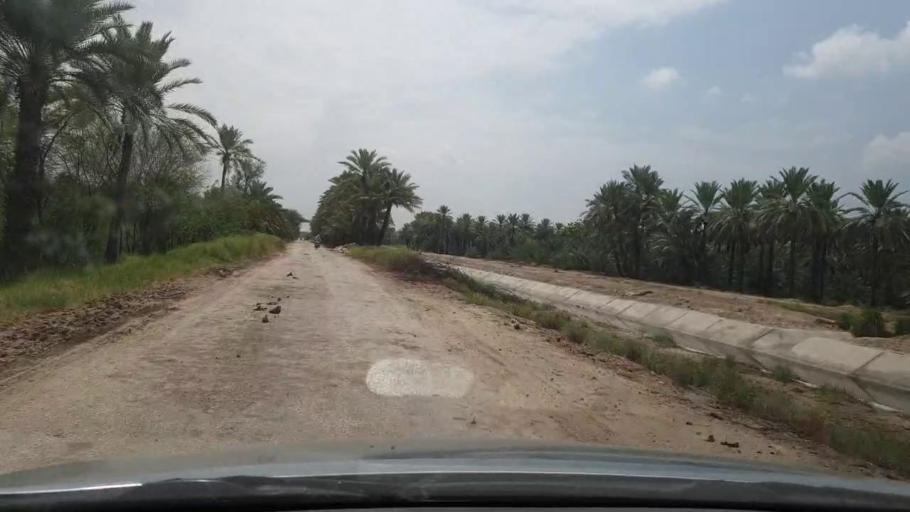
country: PK
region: Sindh
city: Khairpur
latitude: 27.4286
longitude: 68.7811
